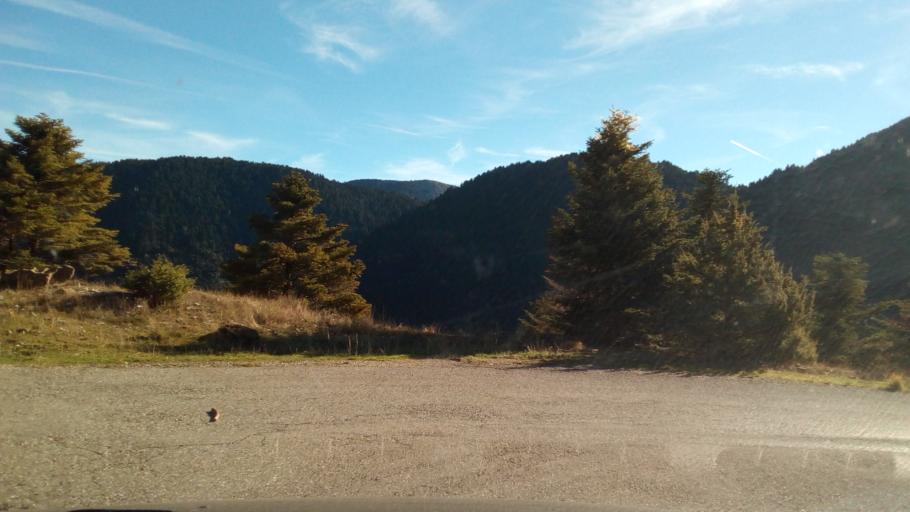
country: GR
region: West Greece
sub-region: Nomos Aitolias kai Akarnanias
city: Nafpaktos
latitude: 38.5387
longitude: 21.8434
